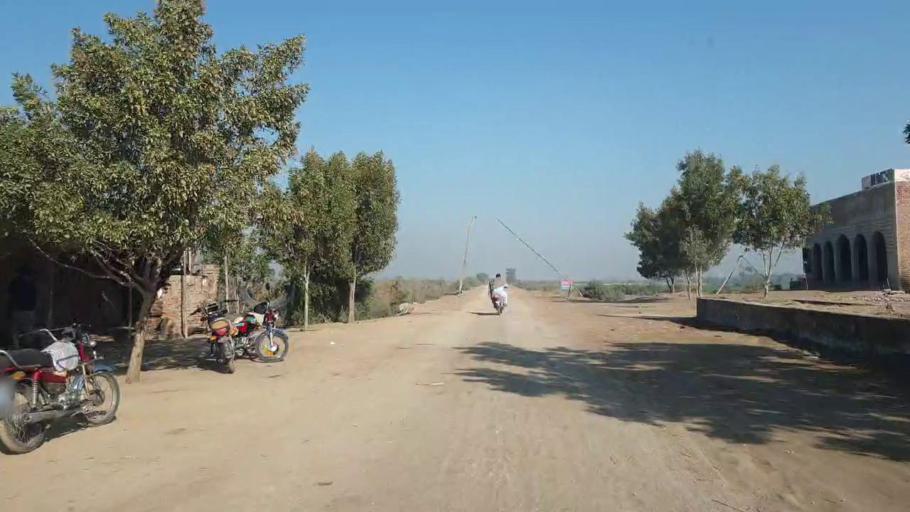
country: PK
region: Sindh
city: Shahdadpur
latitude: 25.9686
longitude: 68.4986
